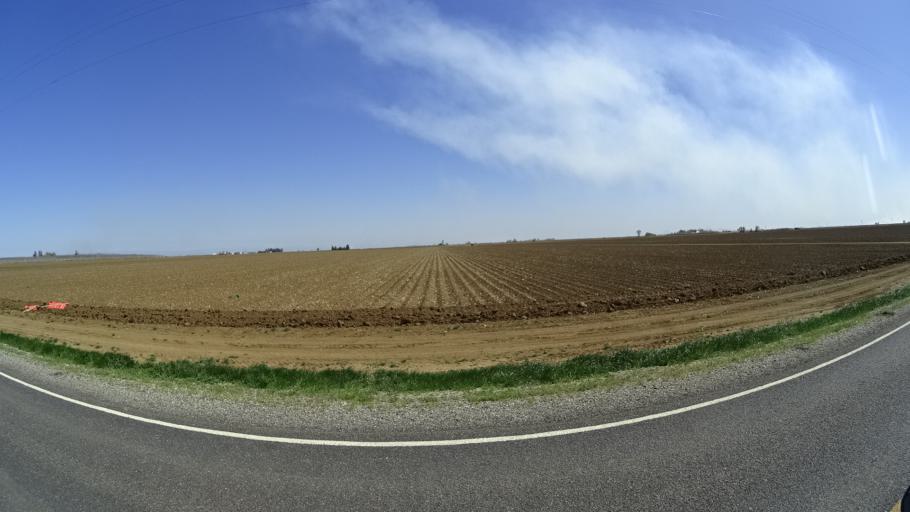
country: US
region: California
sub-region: Glenn County
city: Willows
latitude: 39.4421
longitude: -122.2487
